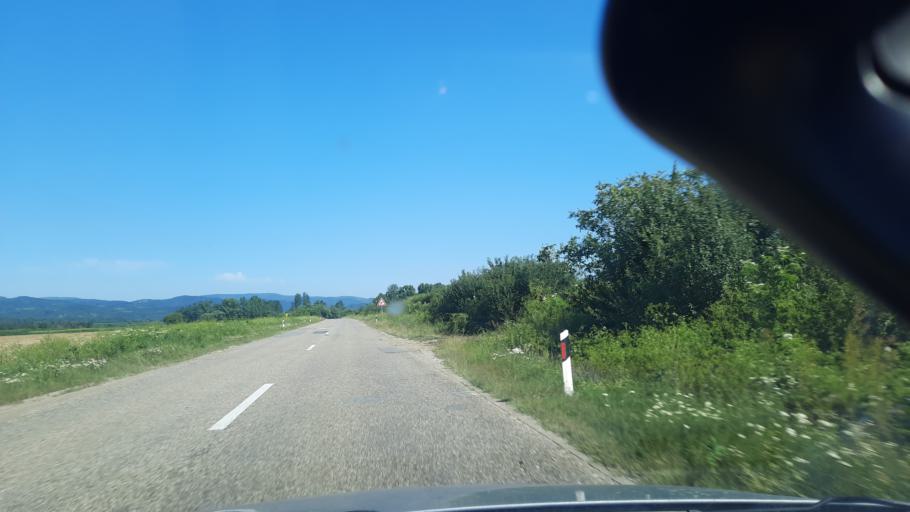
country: RS
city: Turija
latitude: 44.5652
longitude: 21.5267
